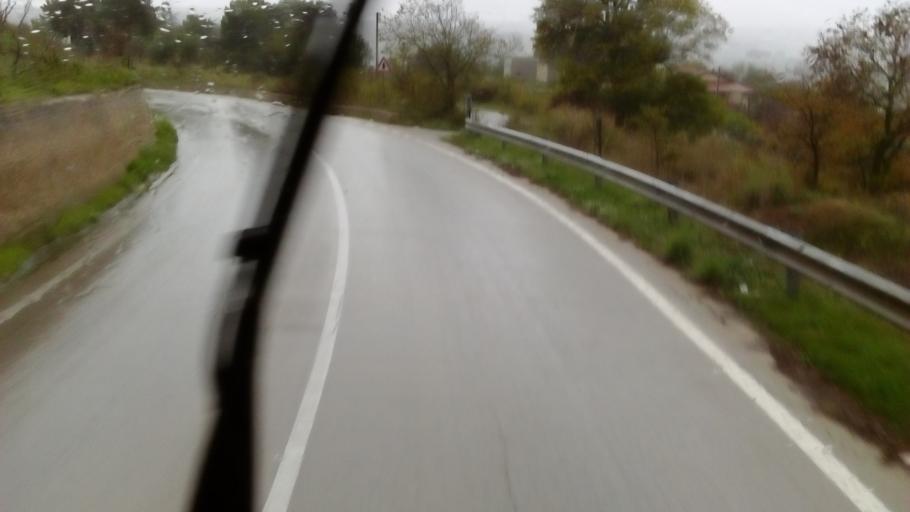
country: IT
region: Sicily
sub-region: Enna
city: Pietraperzia
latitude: 37.4274
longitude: 14.1667
